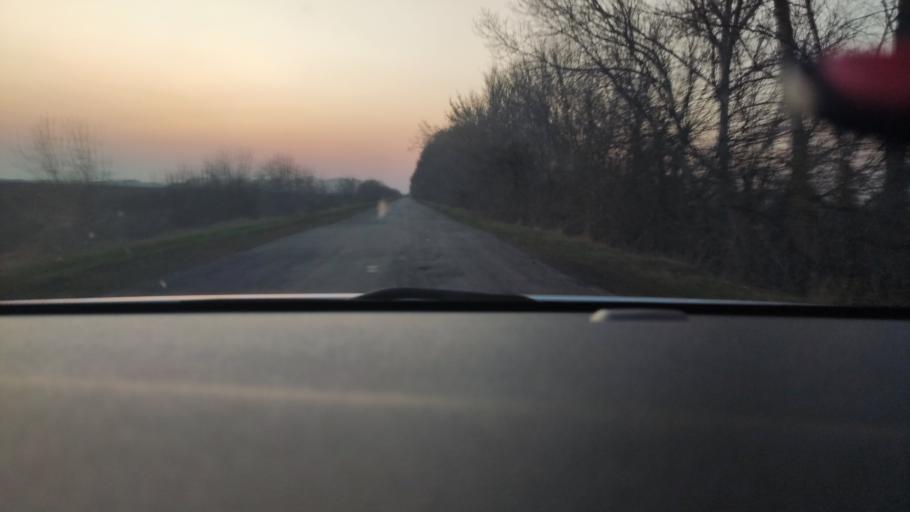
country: RU
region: Voronezj
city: Uryv-Pokrovka
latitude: 51.1293
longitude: 39.1053
